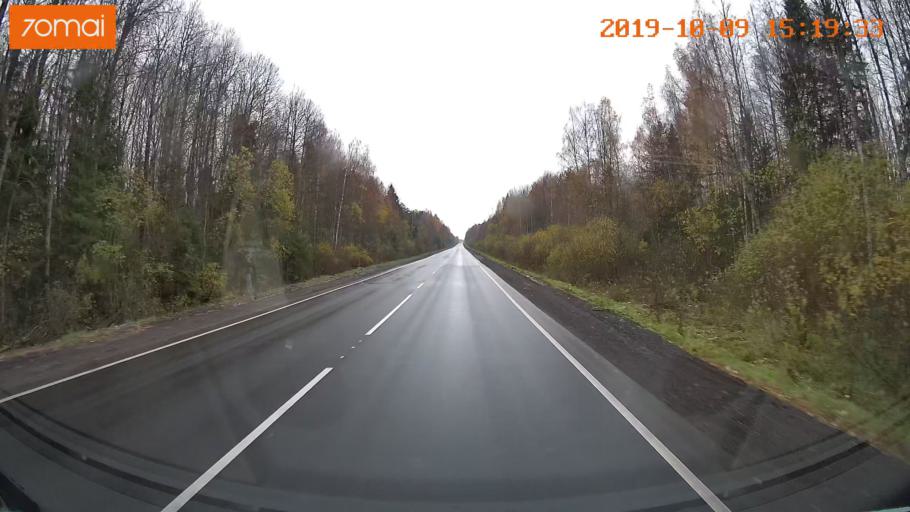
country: RU
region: Kostroma
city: Susanino
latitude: 58.0743
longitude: 41.5542
